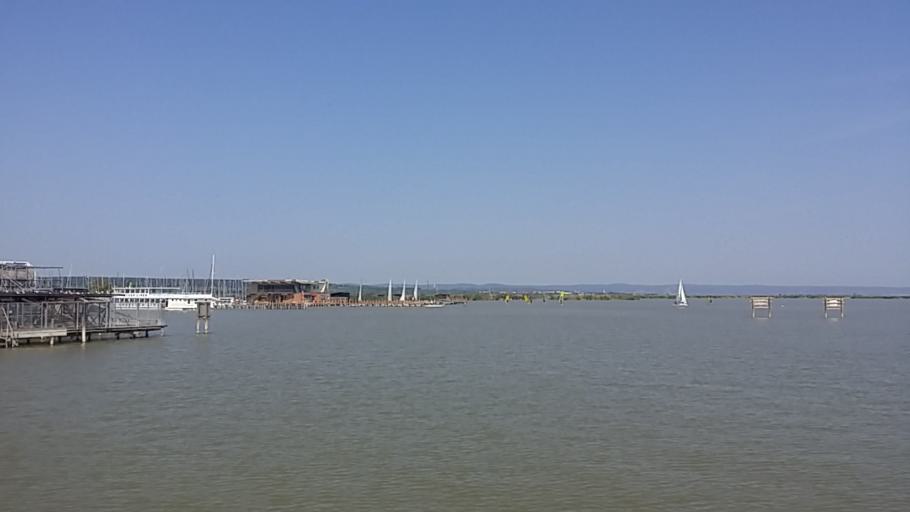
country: AT
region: Burgenland
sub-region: Eisenstadt-Umgebung
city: Morbisch am See
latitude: 47.7538
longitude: 16.7011
